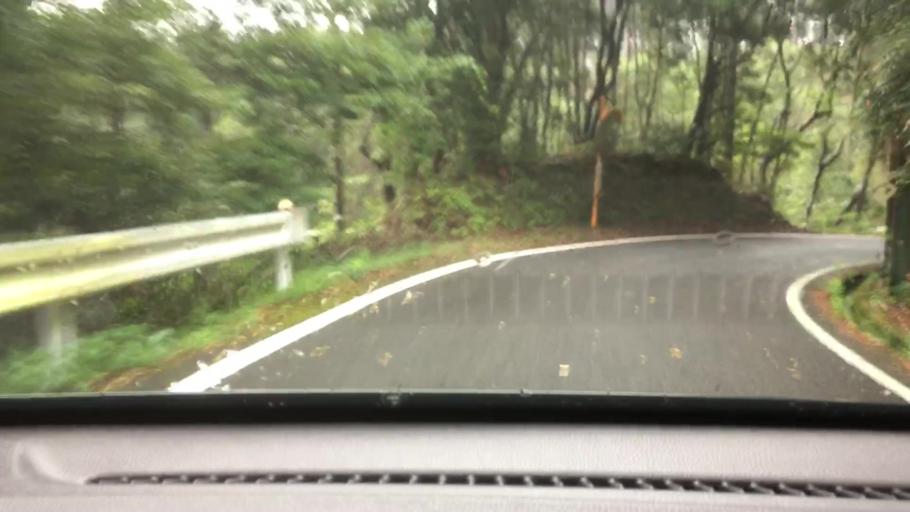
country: JP
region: Nagasaki
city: Togitsu
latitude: 32.9173
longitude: 129.7261
